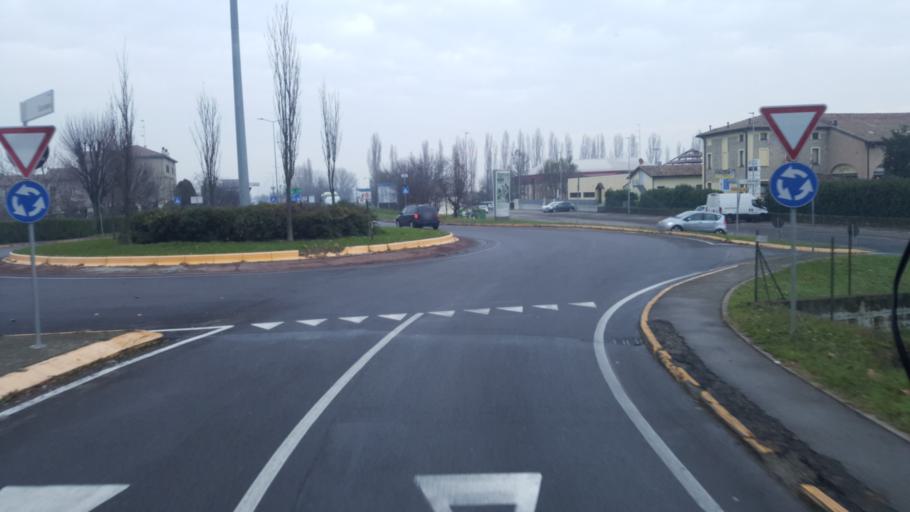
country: IT
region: Emilia-Romagna
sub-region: Provincia di Parma
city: Parma
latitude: 44.8265
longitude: 10.3292
